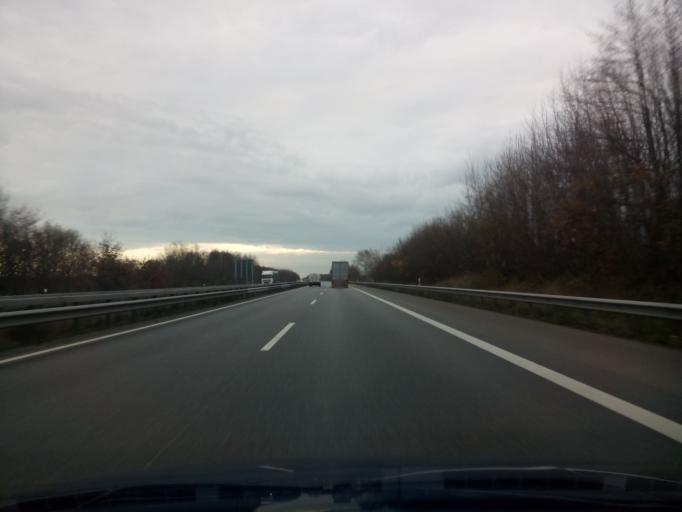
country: DE
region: Lower Saxony
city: Driftsethe
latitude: 53.4336
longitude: 8.5810
